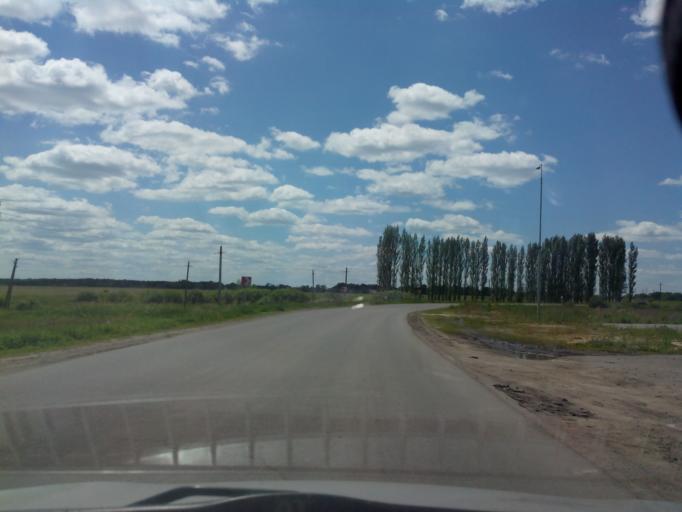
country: RU
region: Voronezj
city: Ternovka
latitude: 51.6767
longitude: 41.5992
